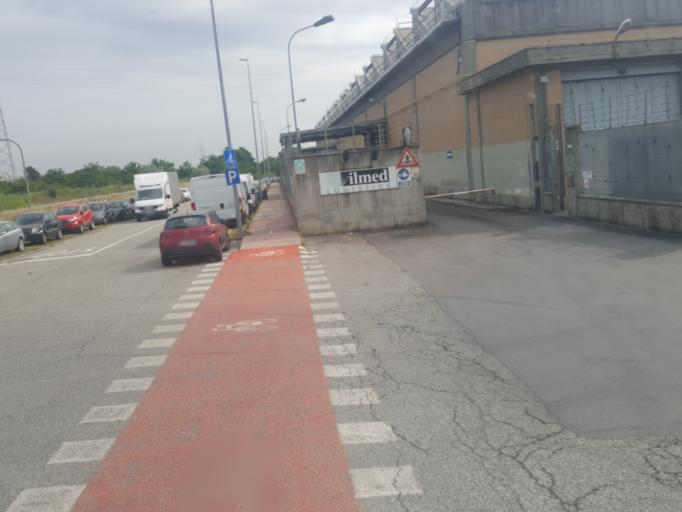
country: IT
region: Piedmont
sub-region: Provincia di Torino
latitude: 44.9480
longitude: 7.5478
